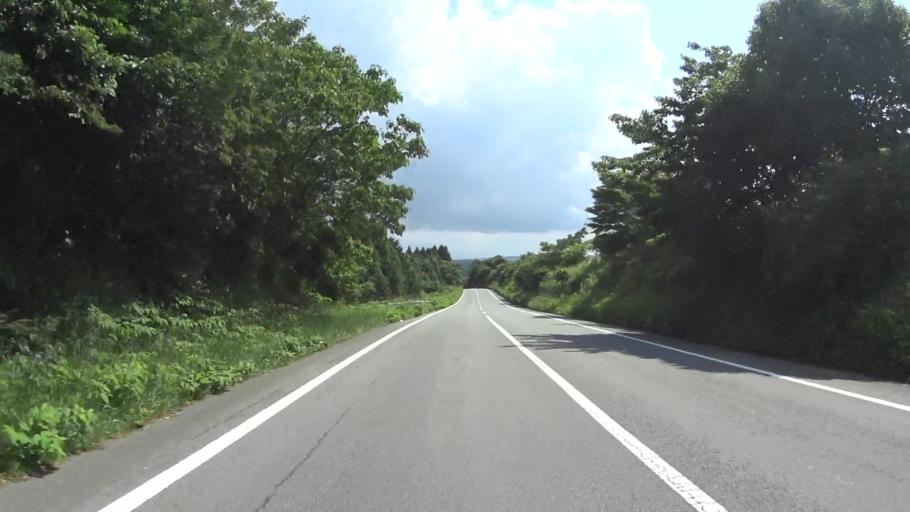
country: JP
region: Kumamoto
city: Aso
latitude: 33.0505
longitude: 131.1698
